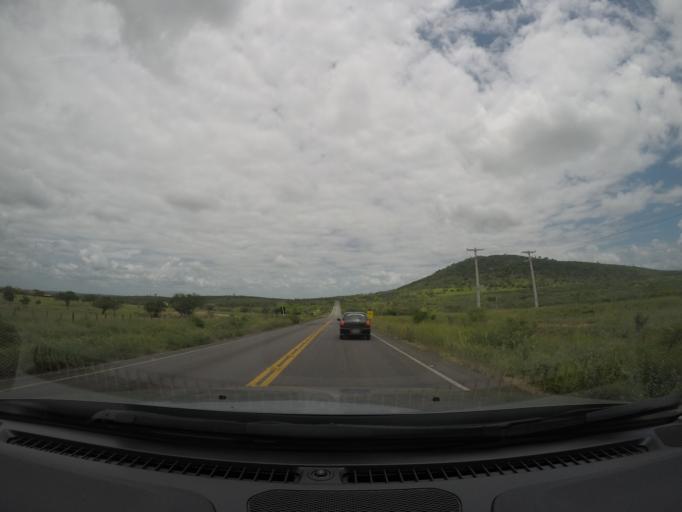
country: BR
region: Bahia
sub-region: Itaberaba
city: Itaberaba
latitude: -12.5032
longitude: -40.2503
